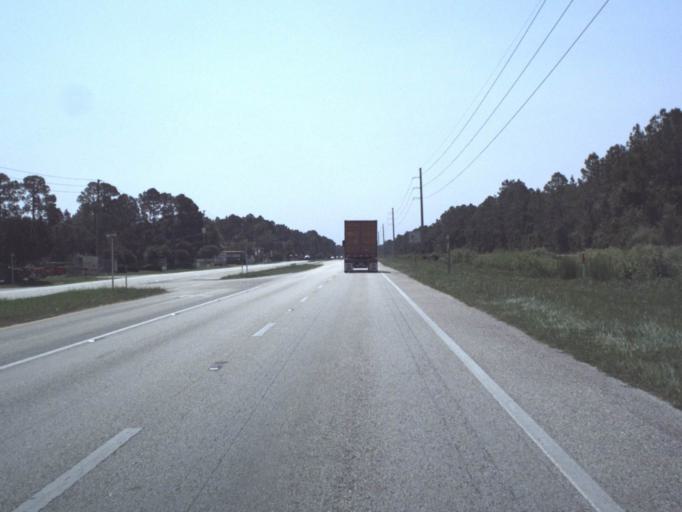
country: US
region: Florida
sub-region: Saint Johns County
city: Villano Beach
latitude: 29.9925
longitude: -81.3742
